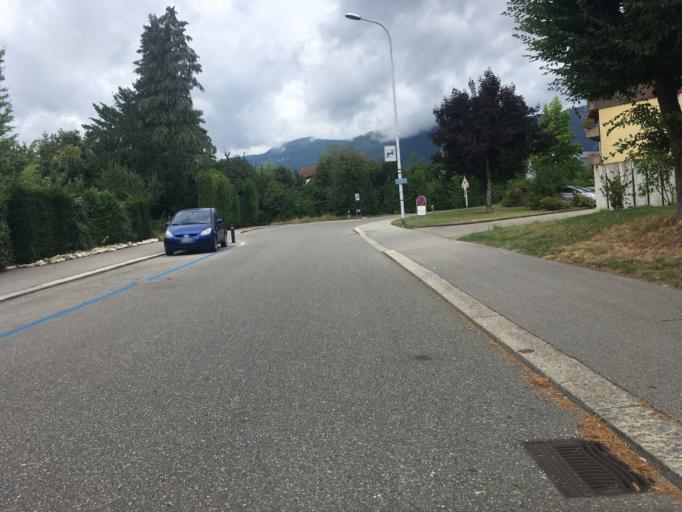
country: CH
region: Solothurn
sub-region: Bezirk Lebern
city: Langendorf
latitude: 47.2145
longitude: 7.5167
